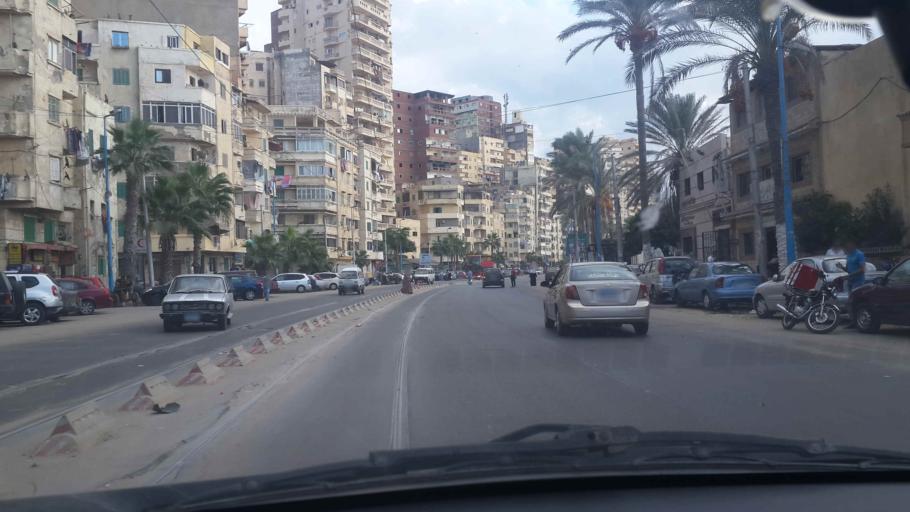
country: EG
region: Alexandria
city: Alexandria
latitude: 31.2091
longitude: 29.8792
